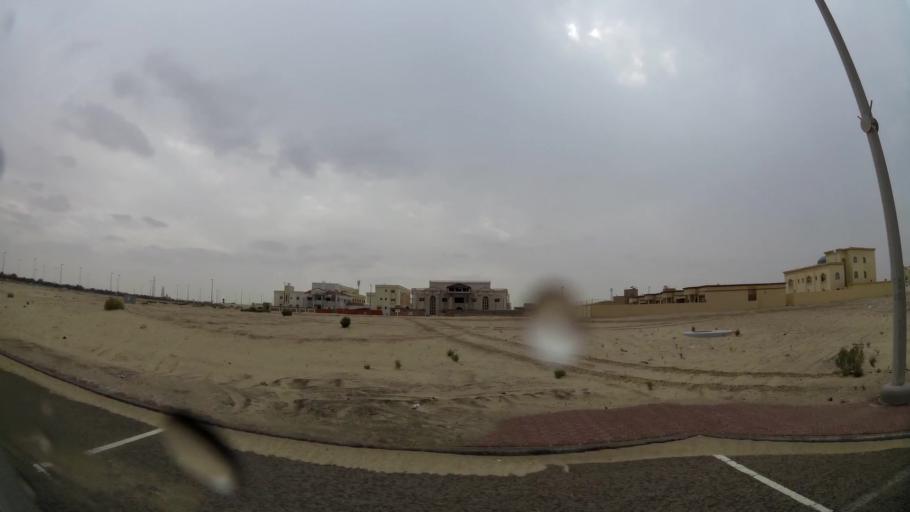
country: AE
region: Abu Dhabi
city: Abu Dhabi
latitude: 24.3652
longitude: 54.6467
